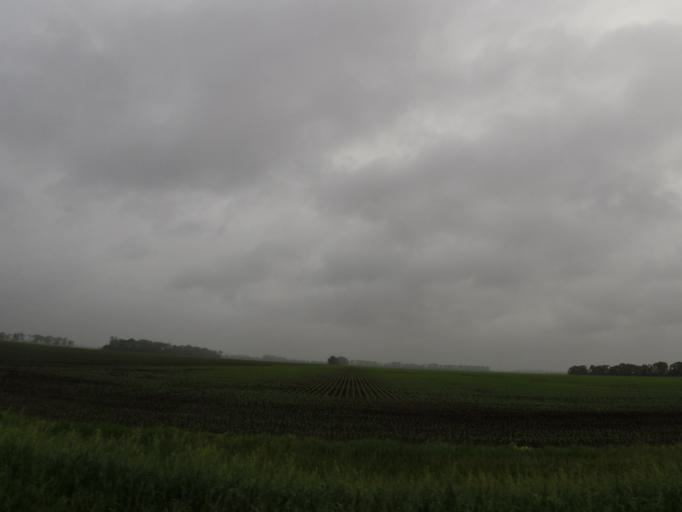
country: US
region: North Dakota
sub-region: Walsh County
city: Grafton
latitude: 48.4632
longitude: -97.2996
